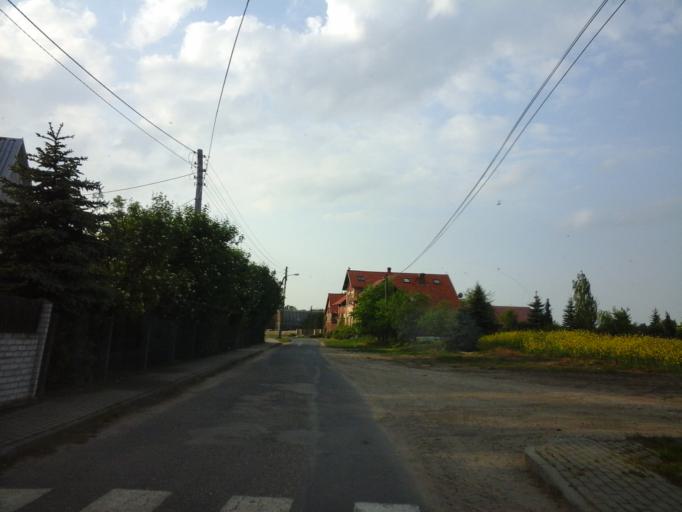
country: PL
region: West Pomeranian Voivodeship
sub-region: Powiat choszczenski
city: Pelczyce
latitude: 52.9876
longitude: 15.3747
